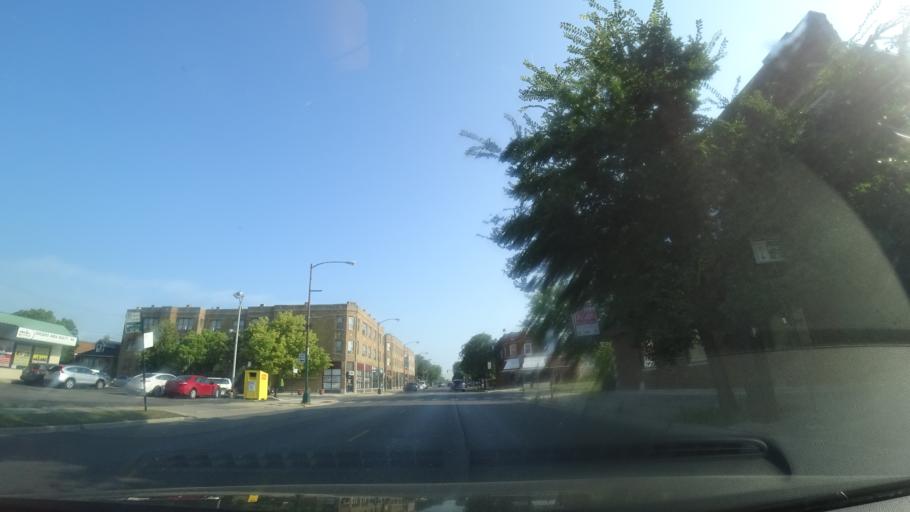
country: US
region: Illinois
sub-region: Cook County
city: Elmwood Park
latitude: 41.9410
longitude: -87.7666
